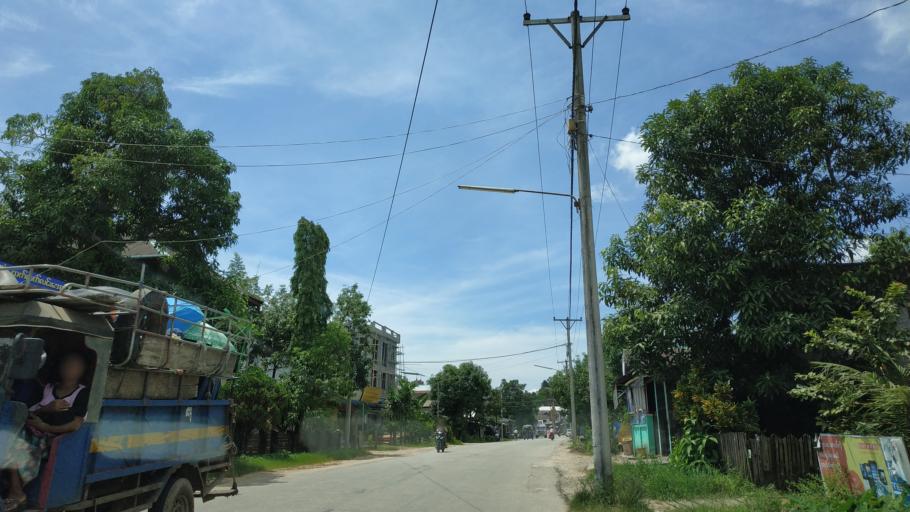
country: MM
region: Tanintharyi
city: Dawei
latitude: 14.1026
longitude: 98.1723
